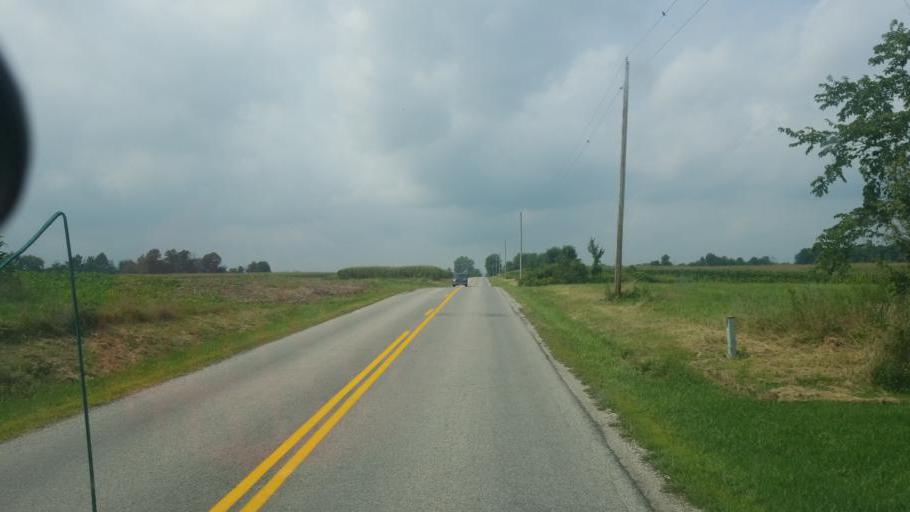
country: US
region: Ohio
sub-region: Huron County
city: Greenwich
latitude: 41.0673
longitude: -82.5442
